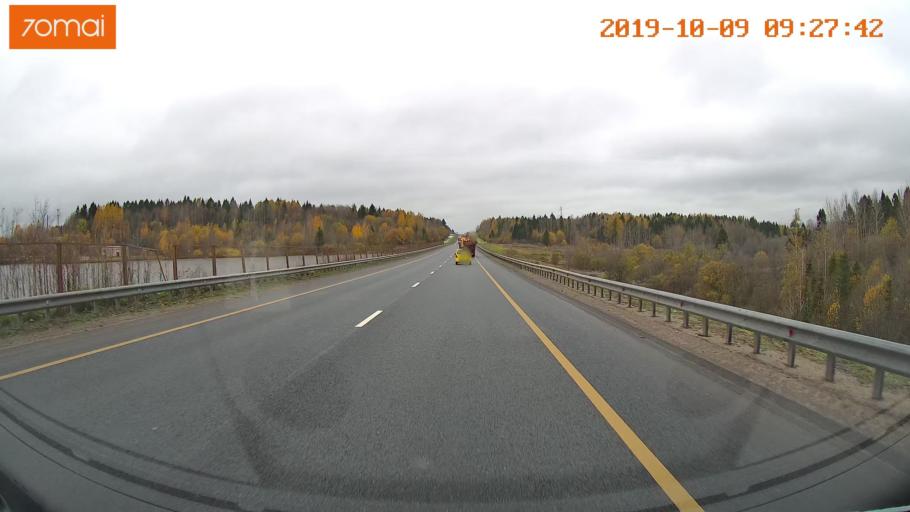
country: RU
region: Vologda
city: Vologda
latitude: 59.1157
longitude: 39.9755
